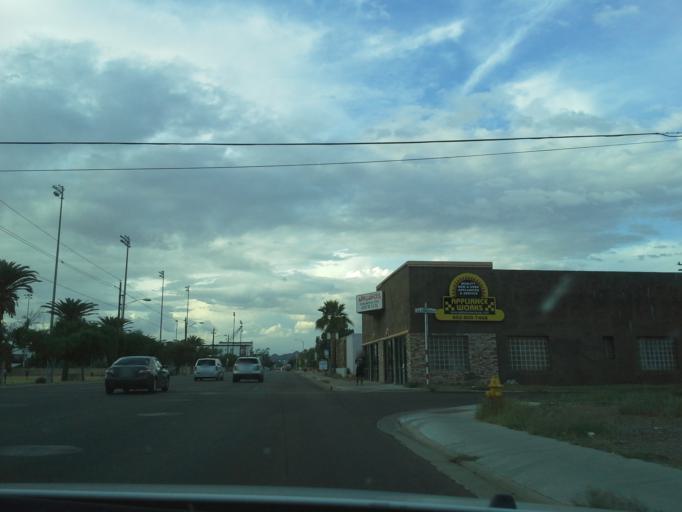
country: US
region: Arizona
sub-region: Maricopa County
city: Phoenix
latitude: 33.4981
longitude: -112.0475
